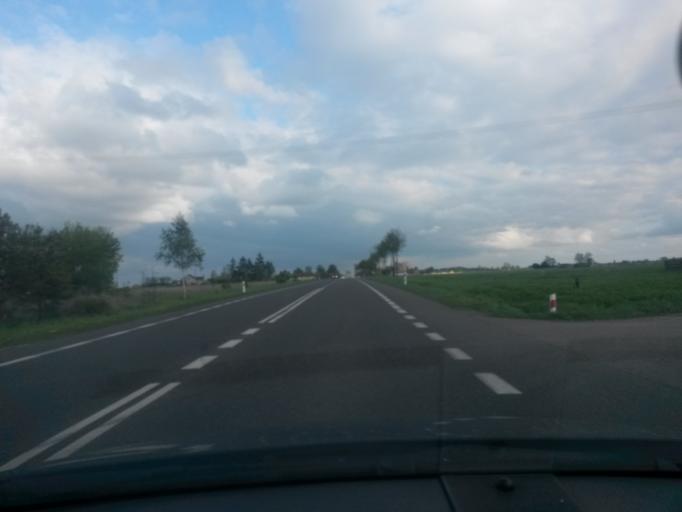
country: PL
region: Masovian Voivodeship
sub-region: Powiat plocki
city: Drobin
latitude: 52.7247
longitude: 20.0111
